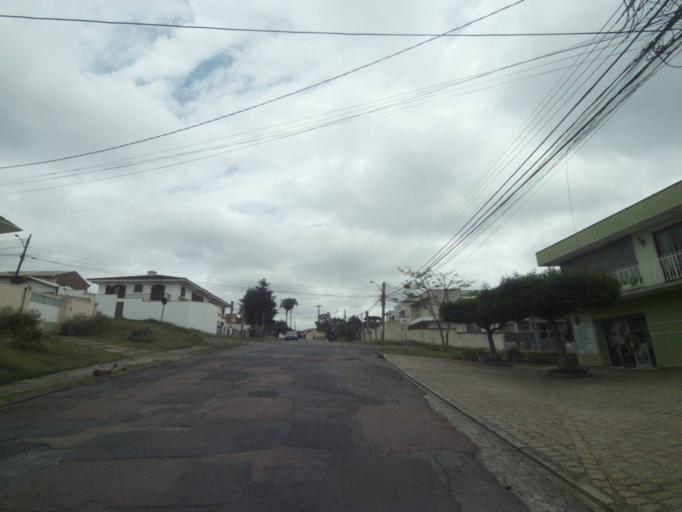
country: BR
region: Parana
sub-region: Curitiba
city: Curitiba
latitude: -25.3884
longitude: -49.2770
